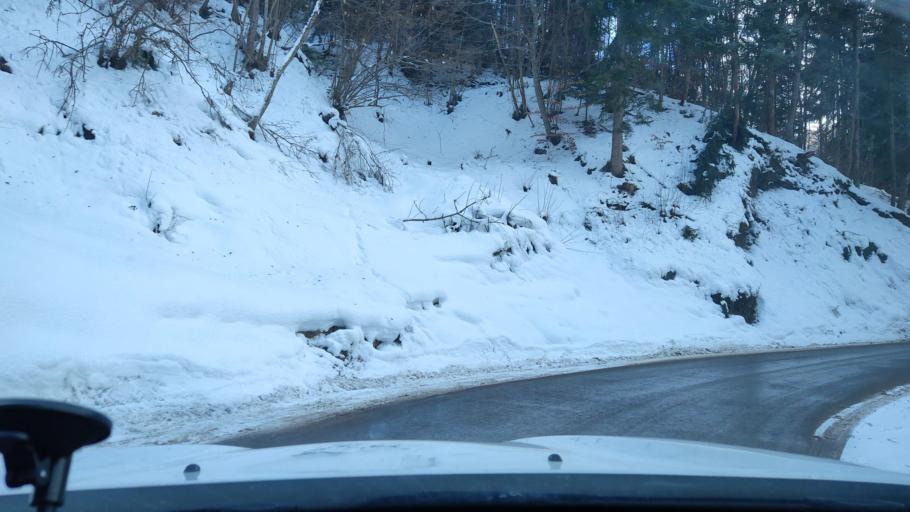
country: FR
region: Rhone-Alpes
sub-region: Departement de la Savoie
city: Saint-Martin-de-Belleville
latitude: 45.4303
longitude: 6.5023
